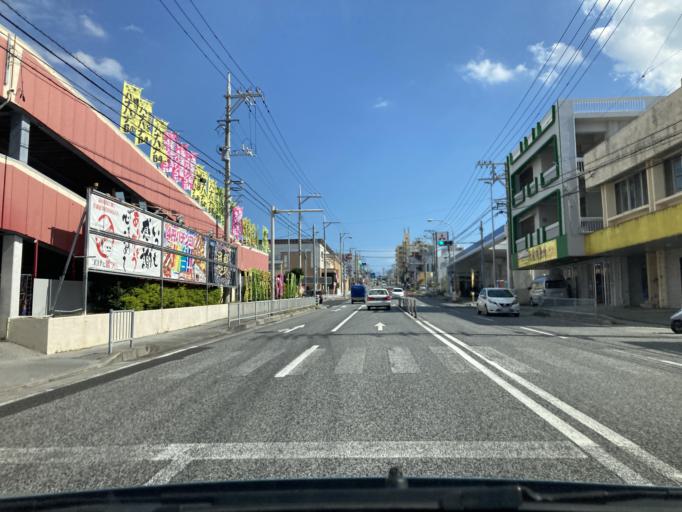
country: JP
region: Okinawa
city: Ginowan
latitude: 26.2591
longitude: 127.7471
